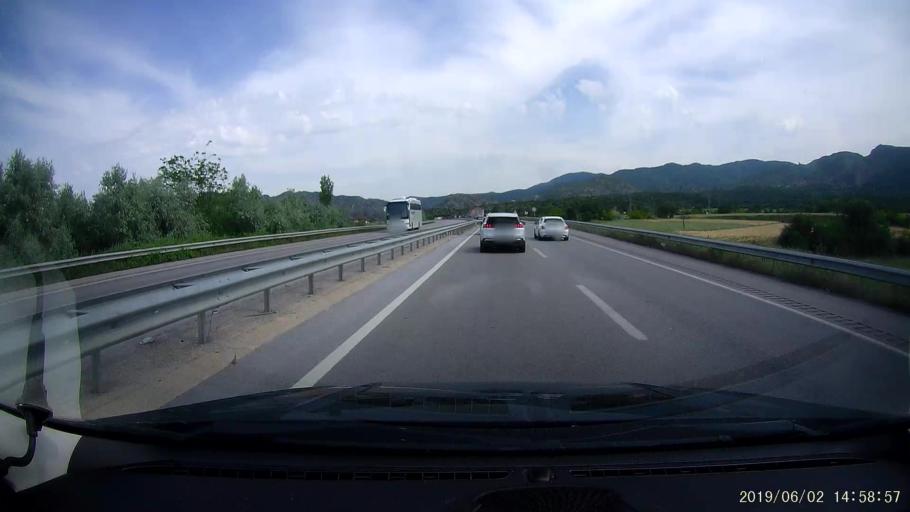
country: TR
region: Corum
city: Osmancik
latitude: 40.9746
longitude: 34.6874
